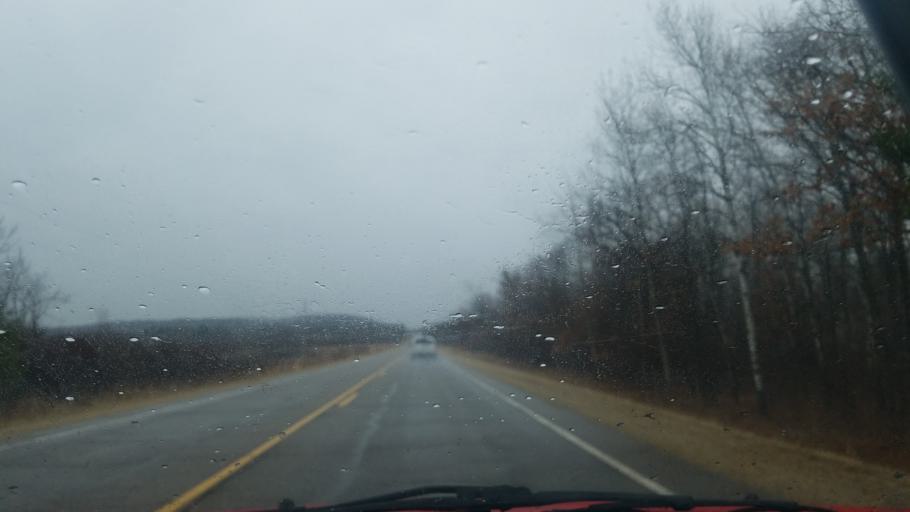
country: US
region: Wisconsin
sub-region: Dunn County
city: Tainter Lake
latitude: 45.0052
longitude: -91.8942
